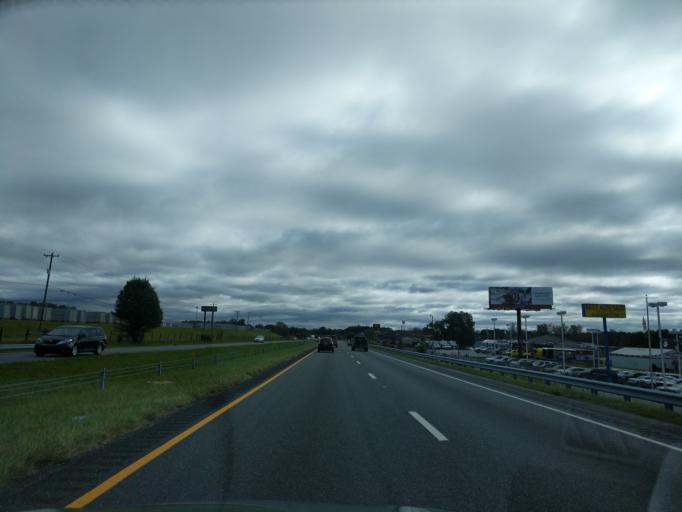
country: US
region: South Carolina
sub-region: Cherokee County
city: East Gaffney
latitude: 35.1024
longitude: -81.6348
